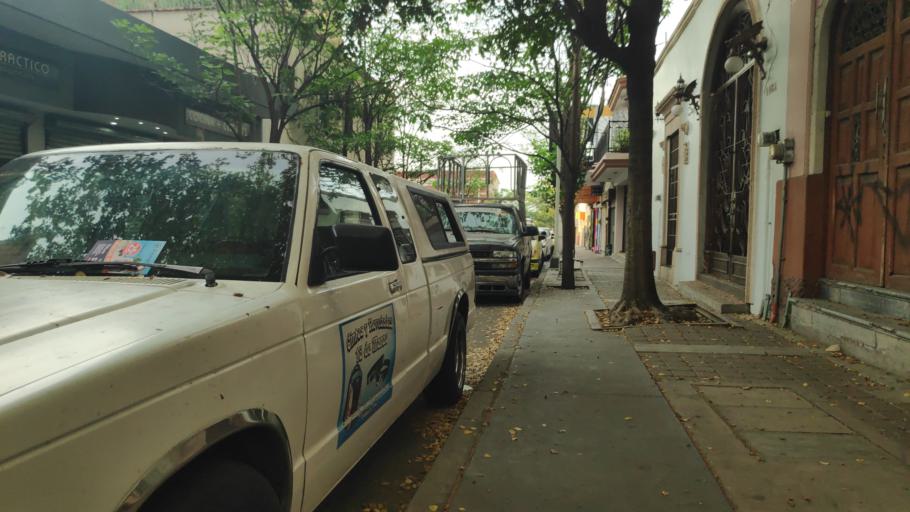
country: MX
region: Sinaloa
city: Culiacan
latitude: 24.8078
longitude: -107.4000
